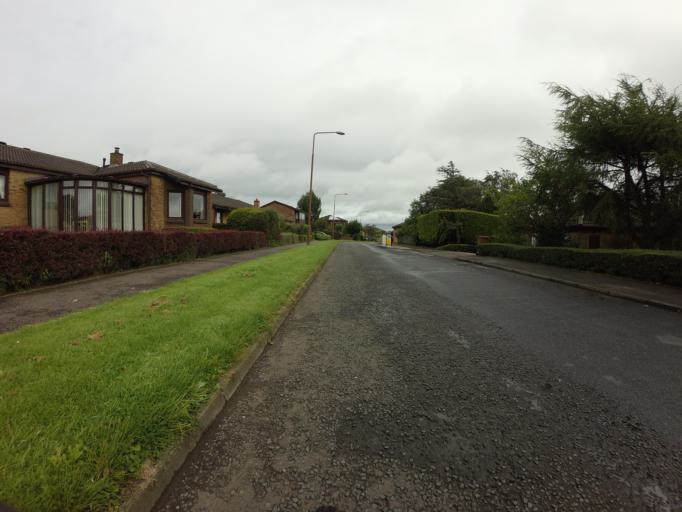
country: GB
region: Scotland
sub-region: West Lothian
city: Livingston
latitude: 55.9105
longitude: -3.5415
